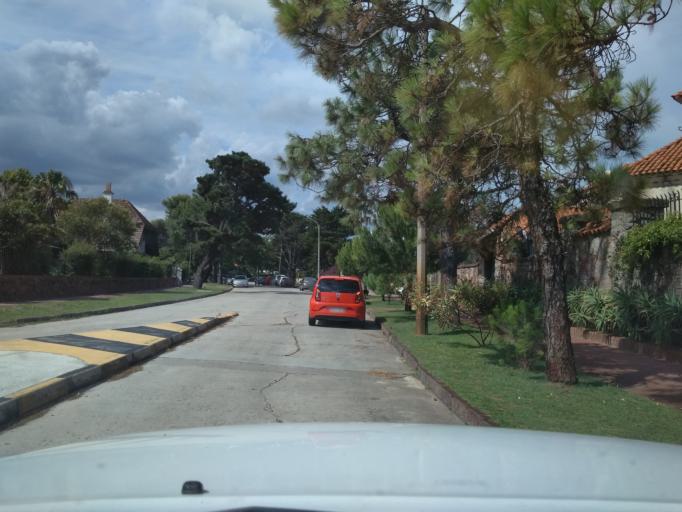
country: UY
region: Canelones
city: Barra de Carrasco
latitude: -34.8898
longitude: -56.0547
